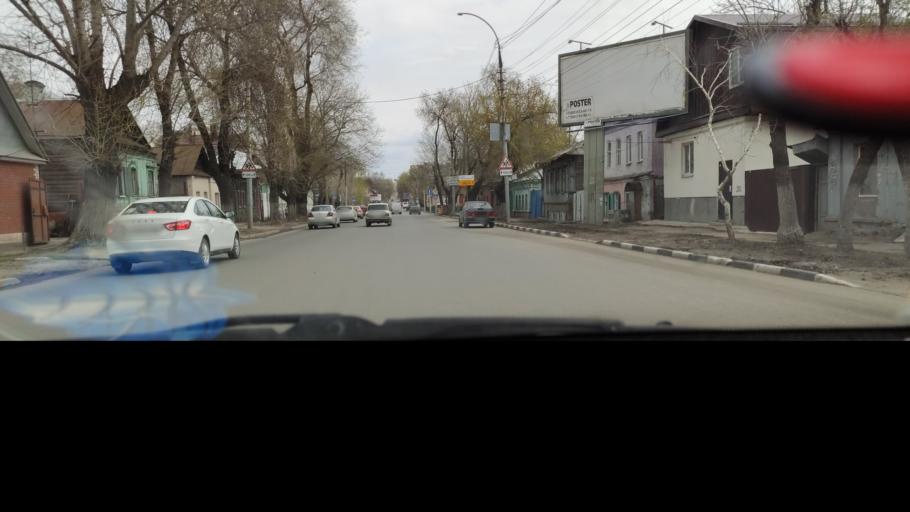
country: RU
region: Saratov
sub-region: Saratovskiy Rayon
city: Saratov
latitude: 51.5398
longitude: 46.0416
